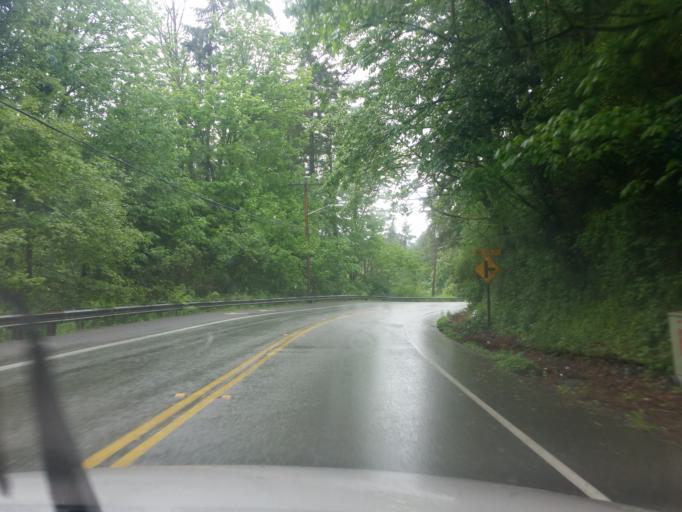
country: US
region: Washington
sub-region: King County
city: Kenmore
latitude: 47.7405
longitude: -122.2501
